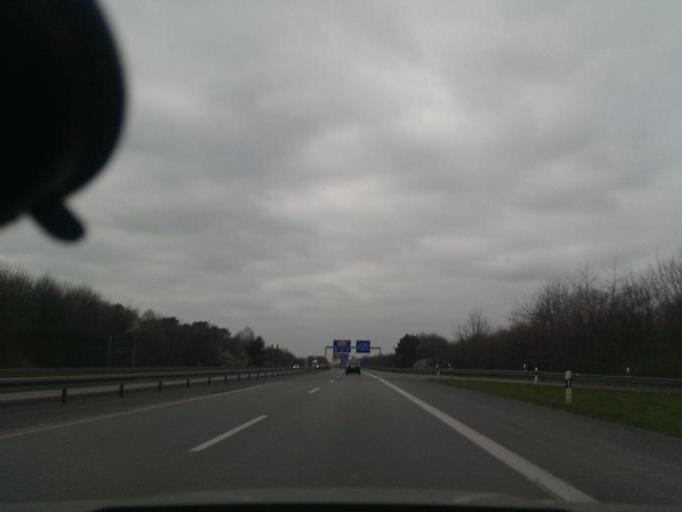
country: DE
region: North Rhine-Westphalia
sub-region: Regierungsbezirk Detmold
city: Rheda-Wiedenbruck
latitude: 51.8509
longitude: 8.3285
